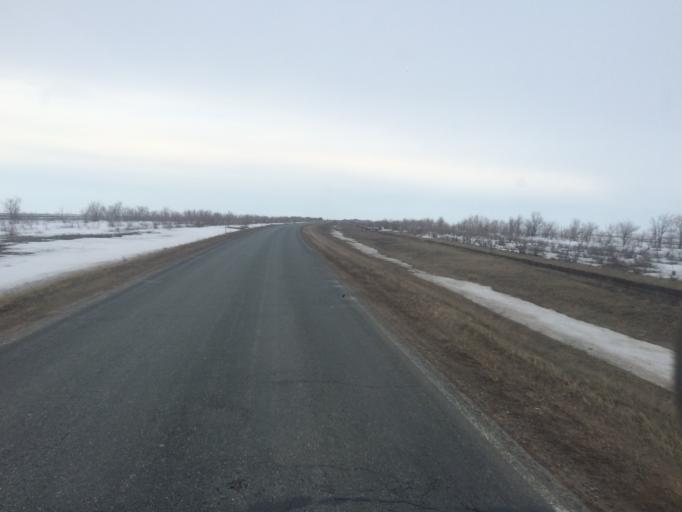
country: KZ
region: Batys Qazaqstan
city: Oral
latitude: 51.4342
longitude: 51.2645
